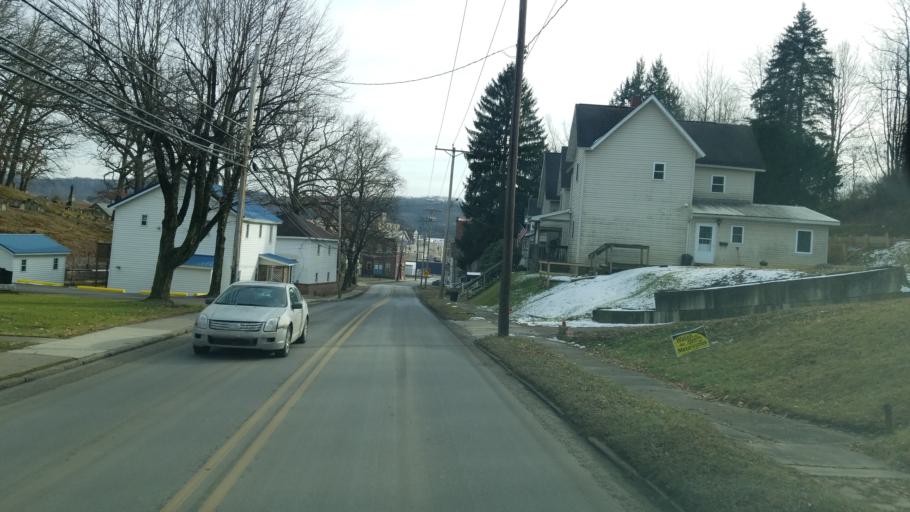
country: US
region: Pennsylvania
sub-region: Jefferson County
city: Punxsutawney
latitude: 40.9476
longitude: -78.9737
